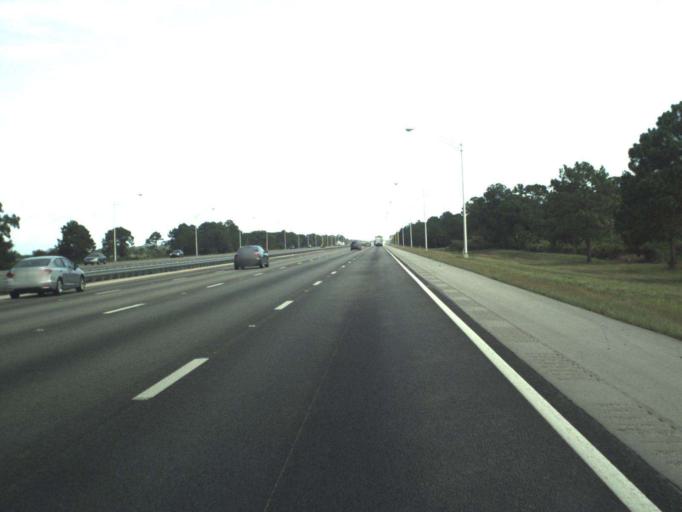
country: US
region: Florida
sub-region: Saint Lucie County
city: Lakewood Park
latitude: 27.4826
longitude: -80.4340
